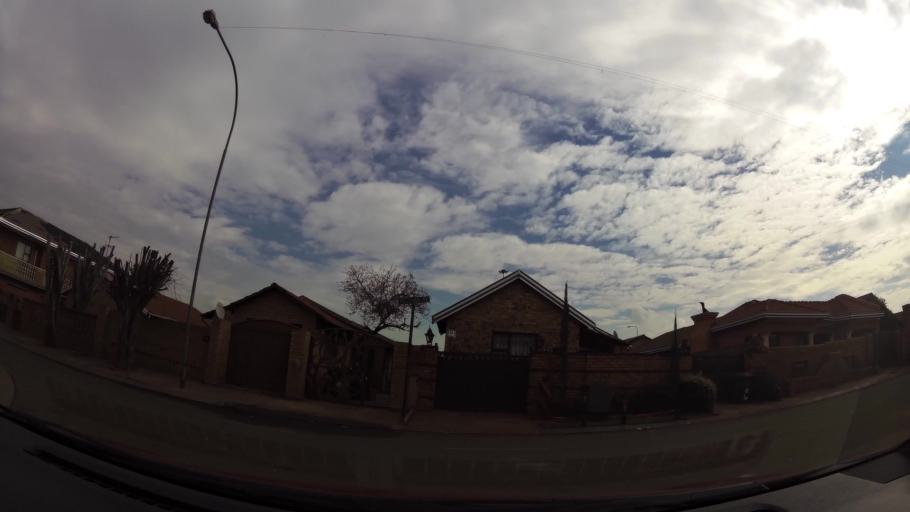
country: ZA
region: Gauteng
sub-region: City of Johannesburg Metropolitan Municipality
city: Soweto
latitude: -26.2713
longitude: 27.8272
